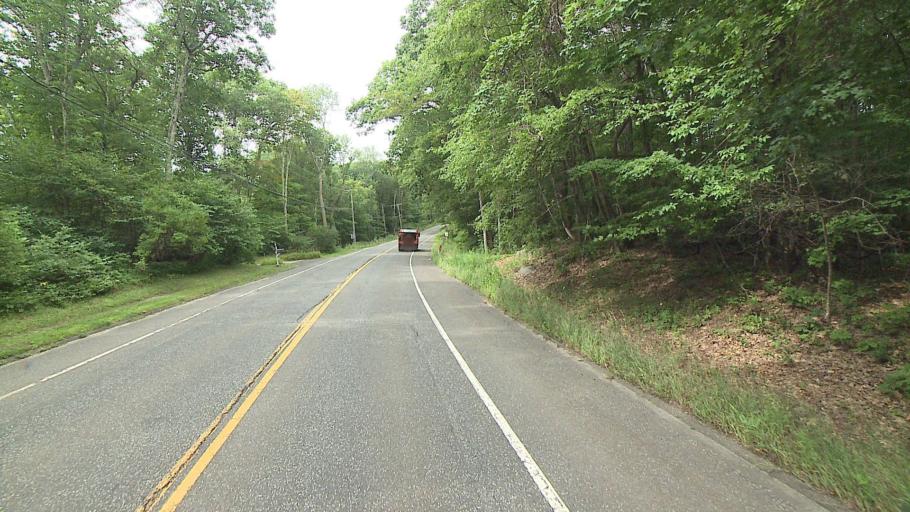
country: US
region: Connecticut
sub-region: Litchfield County
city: New Preston
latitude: 41.7368
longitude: -73.3982
